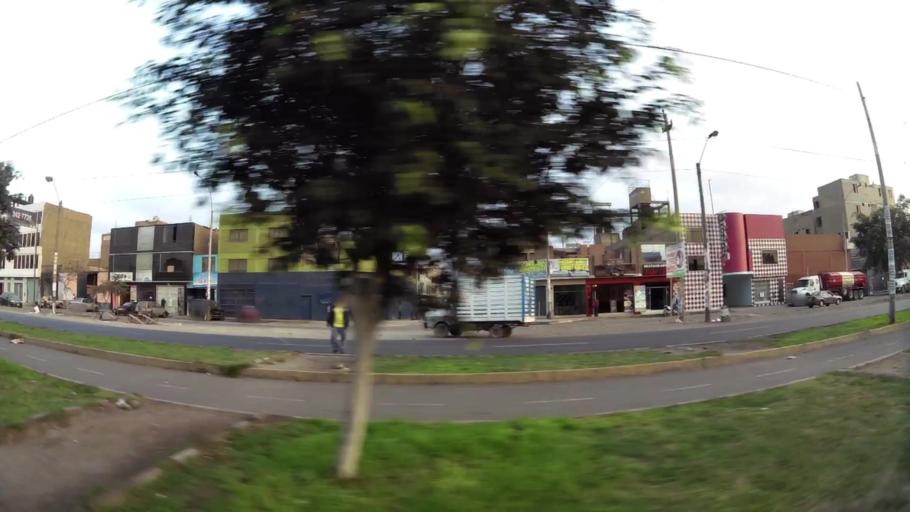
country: PE
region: Lima
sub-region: Lima
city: Independencia
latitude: -12.0127
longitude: -77.0842
